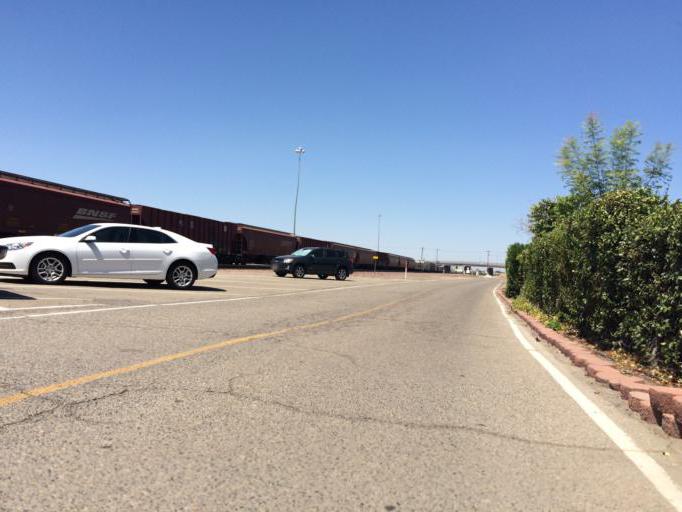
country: US
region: California
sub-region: Fresno County
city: Fresno
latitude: 36.7036
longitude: -119.7600
